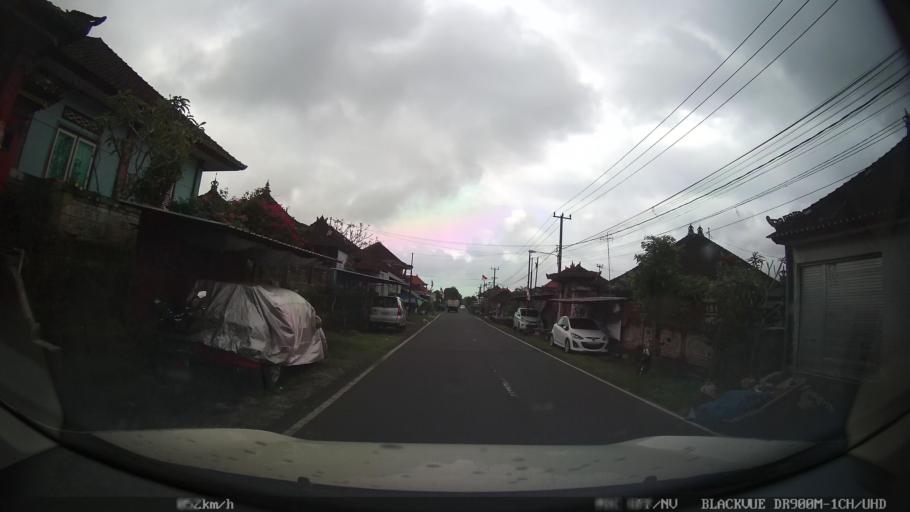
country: ID
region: Bali
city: Empalan
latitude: -8.3994
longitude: 115.1482
